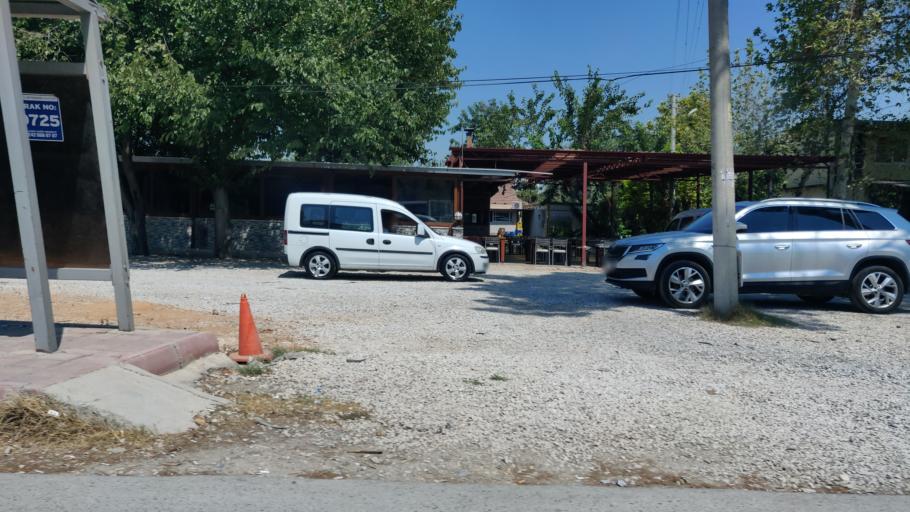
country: TR
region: Antalya
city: Antalya
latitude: 36.9001
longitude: 30.6338
